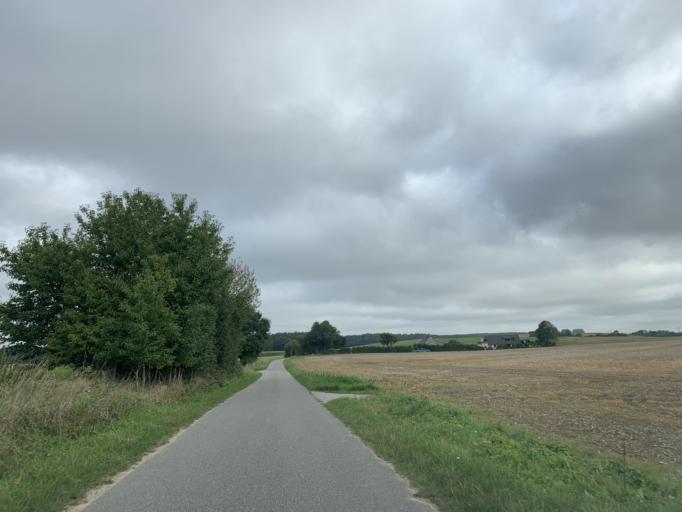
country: DE
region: Mecklenburg-Vorpommern
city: Blankensee
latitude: 53.4175
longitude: 13.2386
